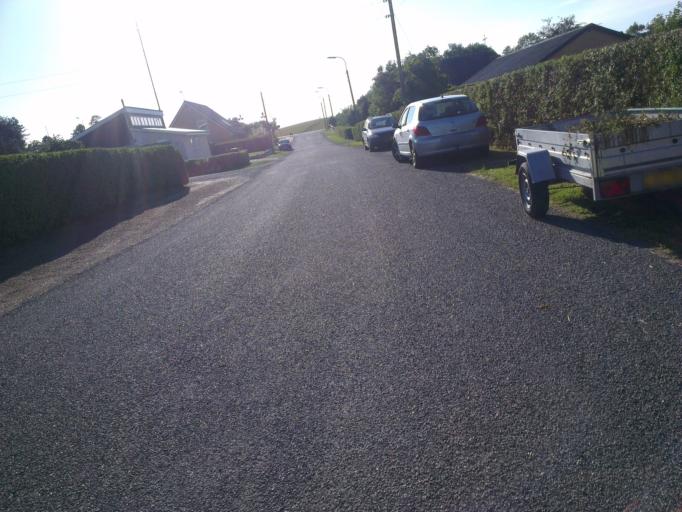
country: DK
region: Capital Region
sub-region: Frederikssund Kommune
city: Skibby
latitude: 55.7930
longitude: 11.9548
